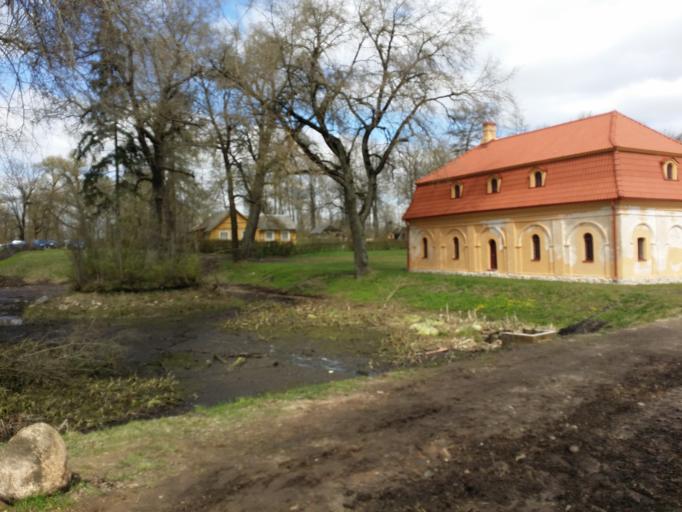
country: LT
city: Nemencine
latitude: 54.8514
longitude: 25.3394
